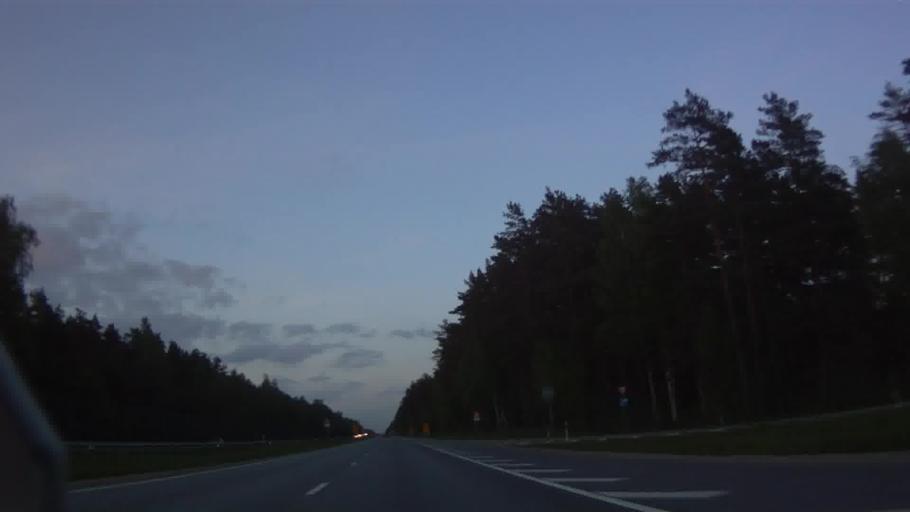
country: LV
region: Riga
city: Bergi
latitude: 57.0117
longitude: 24.3135
